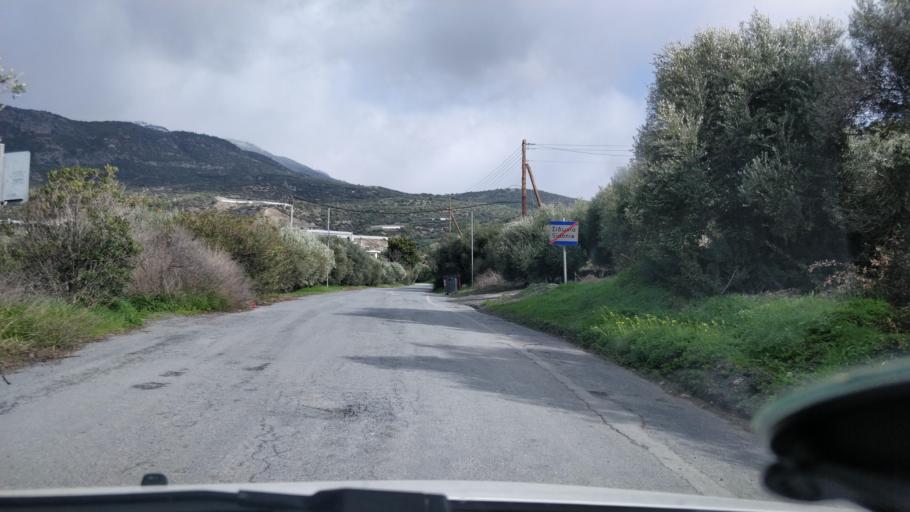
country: GR
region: Crete
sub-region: Nomos Lasithiou
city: Gra Liyia
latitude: 34.9895
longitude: 25.5015
